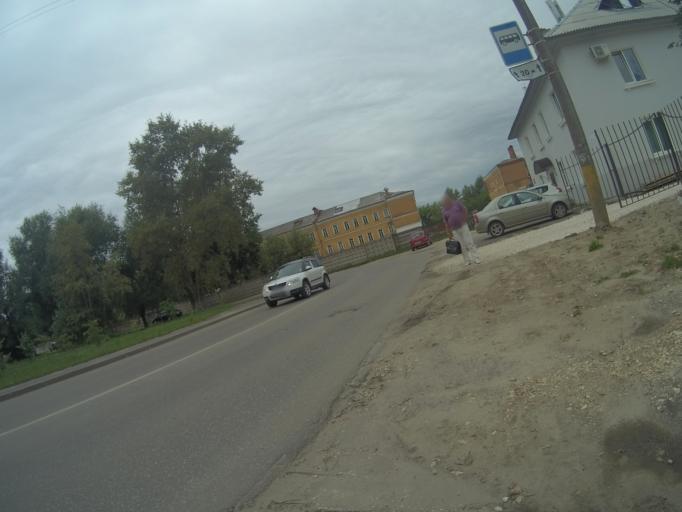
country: RU
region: Vladimir
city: Vladimir
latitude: 56.1259
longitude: 40.3729
